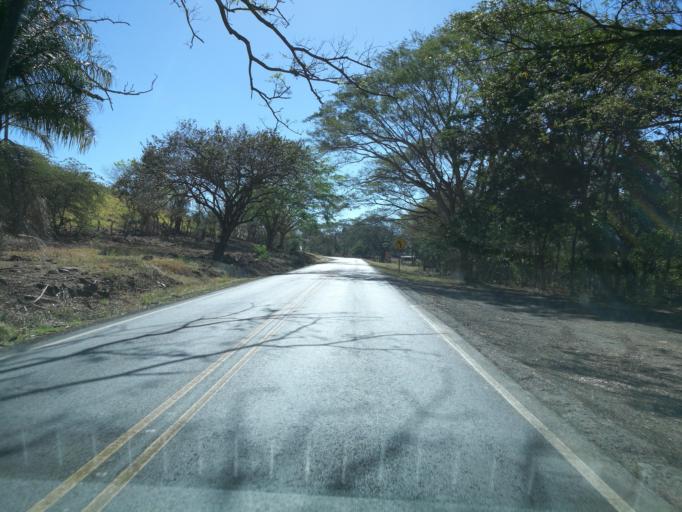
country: CR
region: Puntarenas
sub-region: Canton Central de Puntarenas
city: Puntarenas
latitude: 10.1007
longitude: -84.8701
